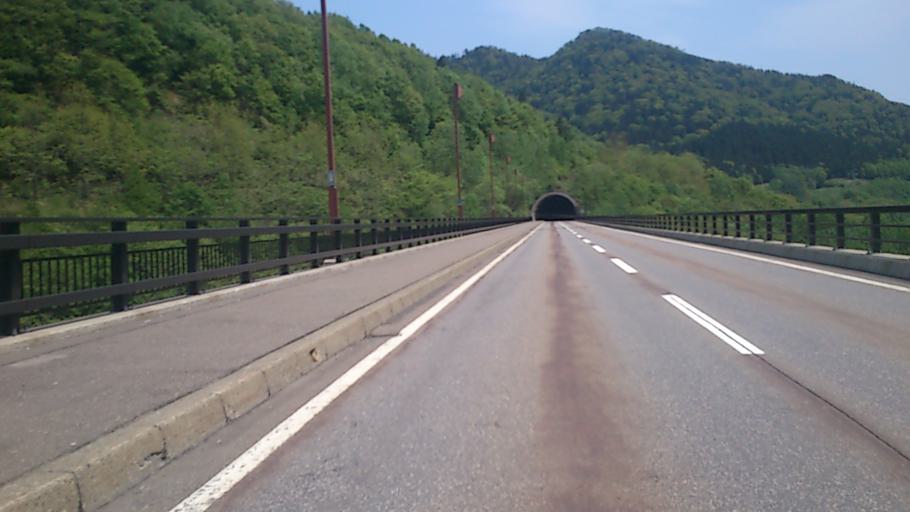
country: JP
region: Hokkaido
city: Otofuke
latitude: 43.3713
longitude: 143.2223
